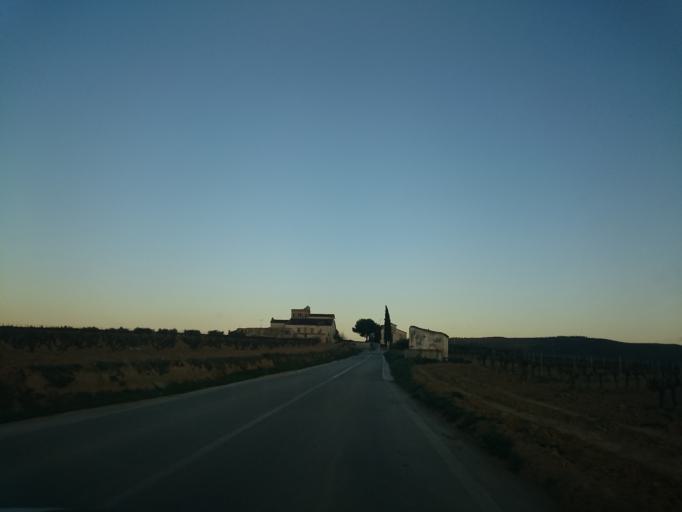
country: ES
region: Catalonia
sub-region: Provincia de Barcelona
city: La Granada
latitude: 41.3531
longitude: 1.7367
